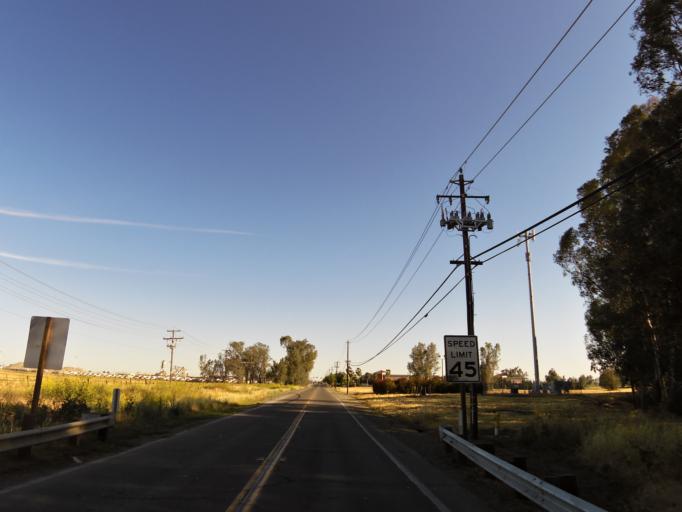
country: US
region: California
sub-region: Merced County
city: Merced
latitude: 37.3215
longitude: -120.5049
